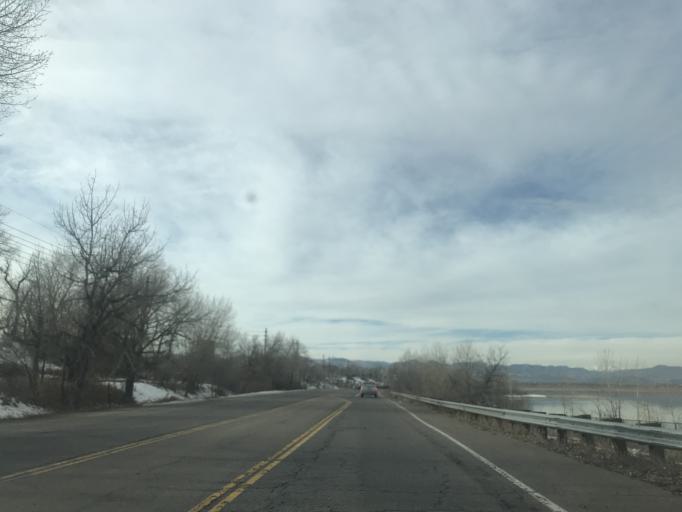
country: US
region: Colorado
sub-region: Douglas County
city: Highlands Ranch
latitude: 39.5647
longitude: -105.0068
